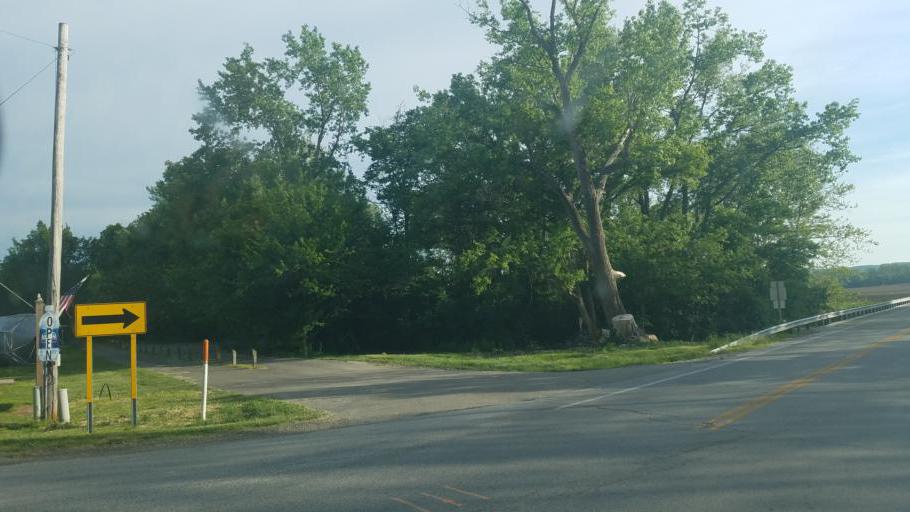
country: US
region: Ohio
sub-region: Ross County
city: Frankfort
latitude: 39.4369
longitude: -83.2222
